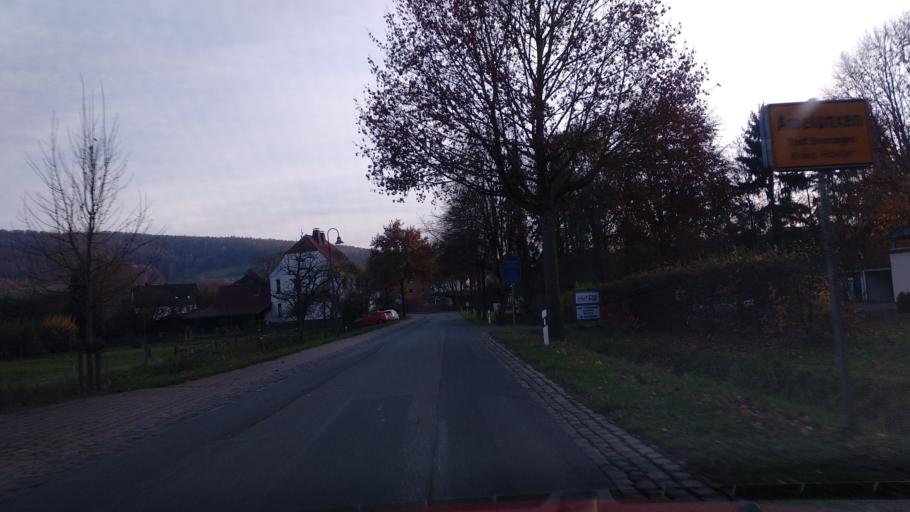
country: DE
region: Lower Saxony
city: Boffzen
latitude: 51.7152
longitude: 9.3429
